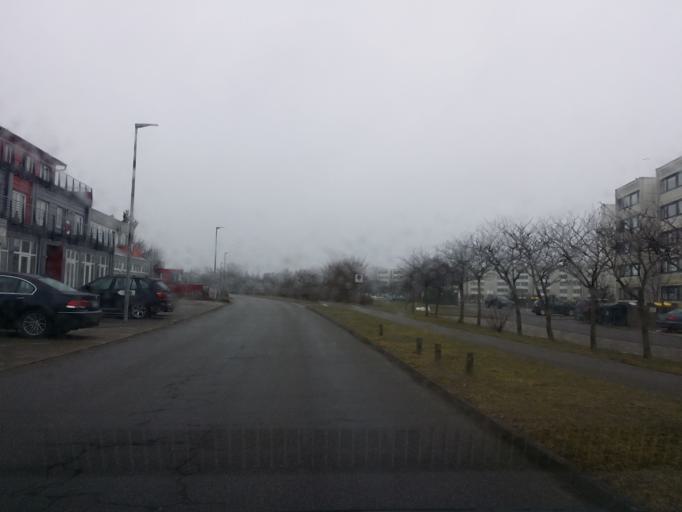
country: DE
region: Schleswig-Holstein
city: Burg auf Fehmarn
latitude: 54.4122
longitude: 11.1966
